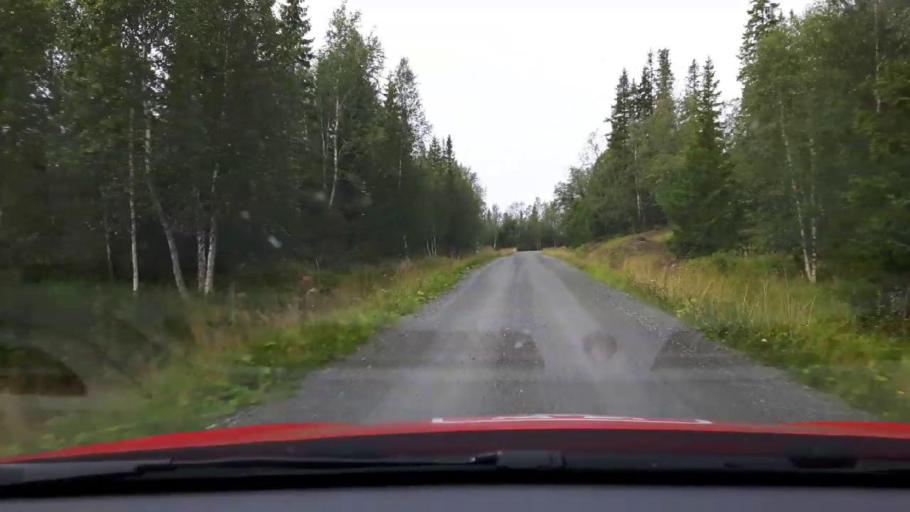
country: SE
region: Jaemtland
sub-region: Are Kommun
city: Are
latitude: 63.7735
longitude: 13.0734
